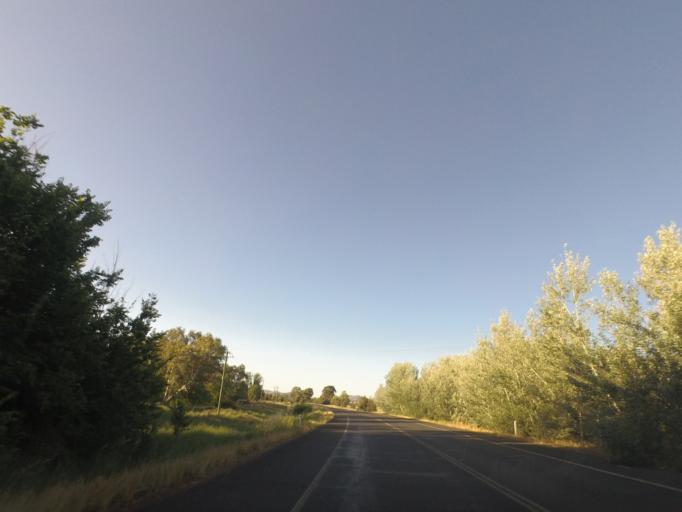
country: AU
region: New South Wales
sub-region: Gundagai
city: Gundagai
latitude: -34.9461
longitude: 148.1691
